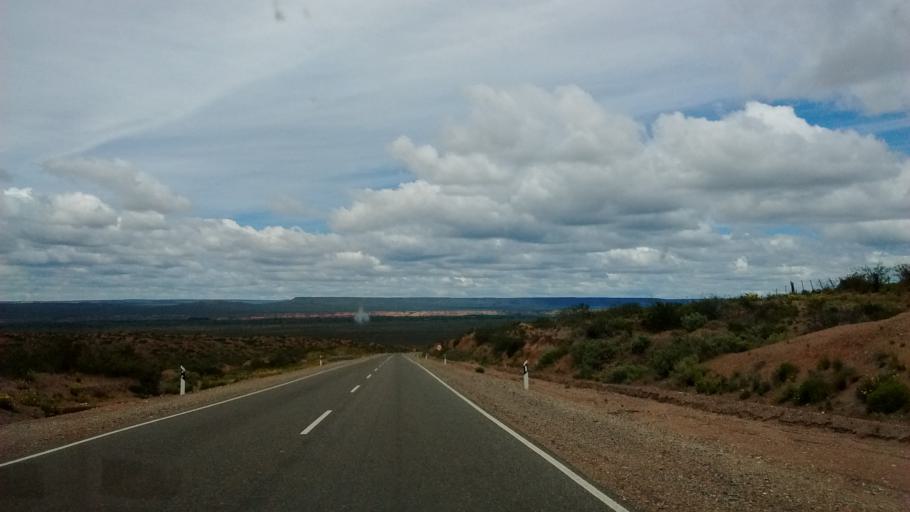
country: AR
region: Neuquen
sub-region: Departamento de Picun Leufu
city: Picun Leufu
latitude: -39.7748
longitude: -69.6533
